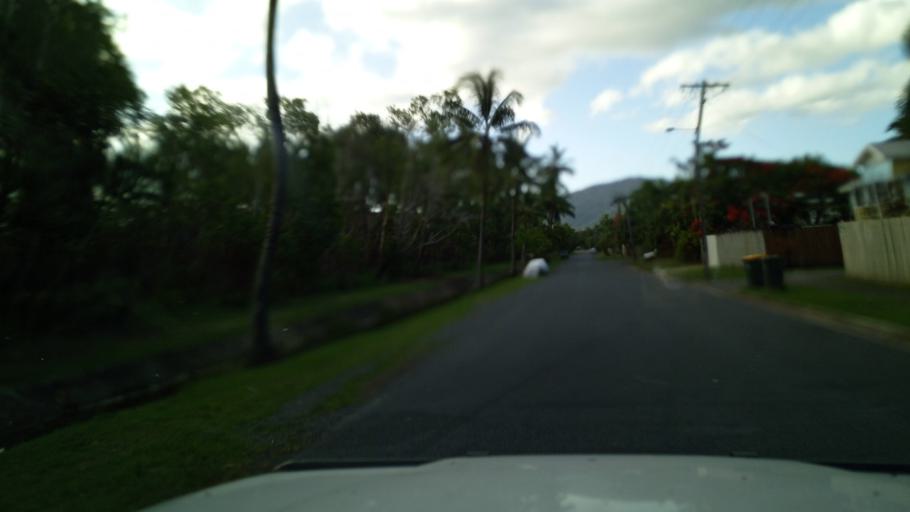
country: AU
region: Queensland
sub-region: Cairns
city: Cairns
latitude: -16.9174
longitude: 145.7551
